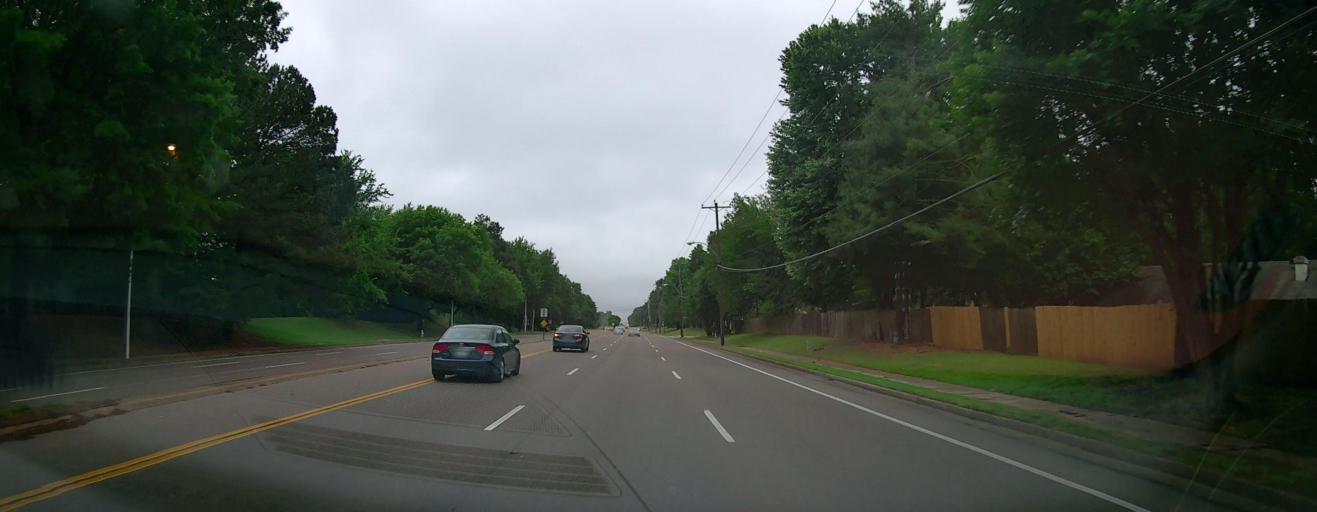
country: US
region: Mississippi
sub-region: De Soto County
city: Olive Branch
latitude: 35.0146
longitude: -89.8313
